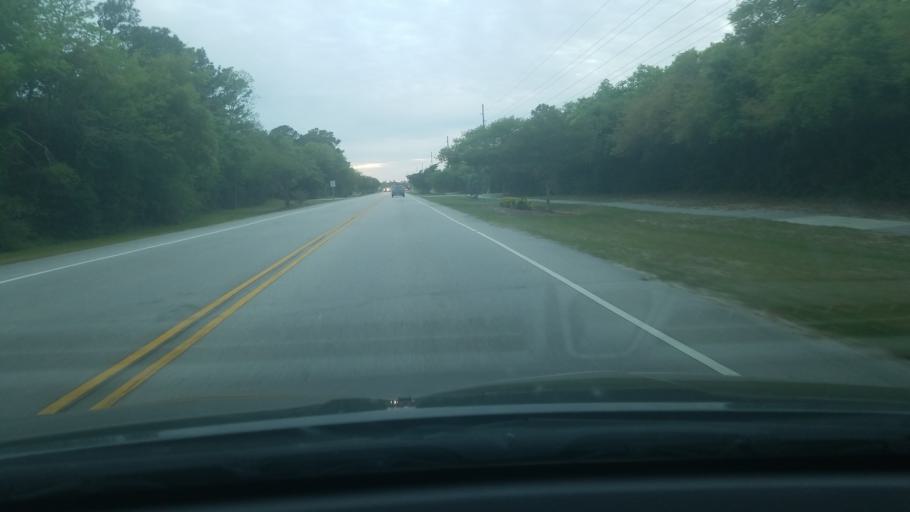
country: US
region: North Carolina
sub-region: Carteret County
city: Cape Carteret
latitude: 34.6628
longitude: -77.0444
